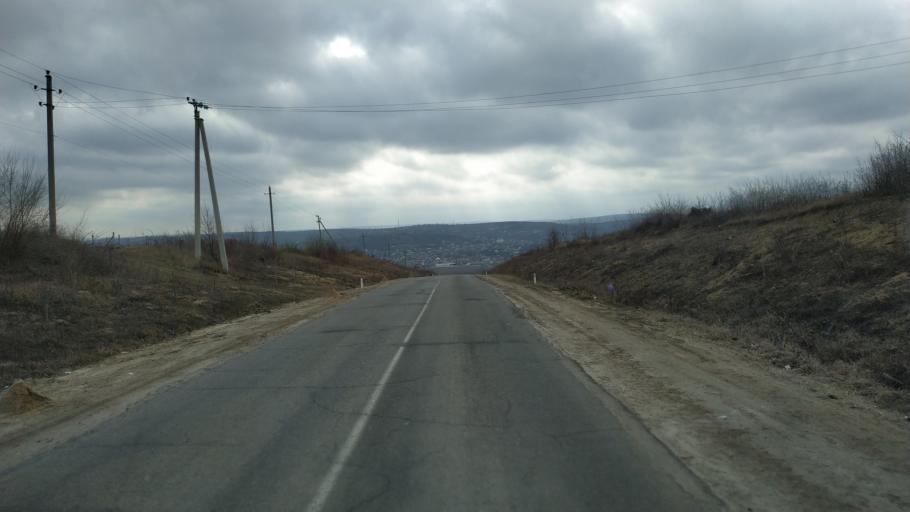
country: MD
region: Laloveni
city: Ialoveni
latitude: 46.8883
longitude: 28.7678
